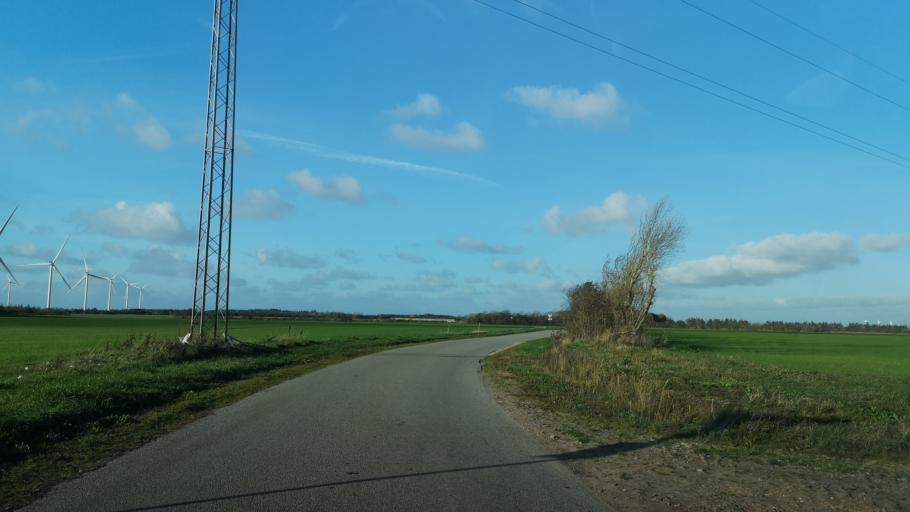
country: DK
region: Central Jutland
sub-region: Ringkobing-Skjern Kommune
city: Skjern
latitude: 55.8421
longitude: 8.3461
